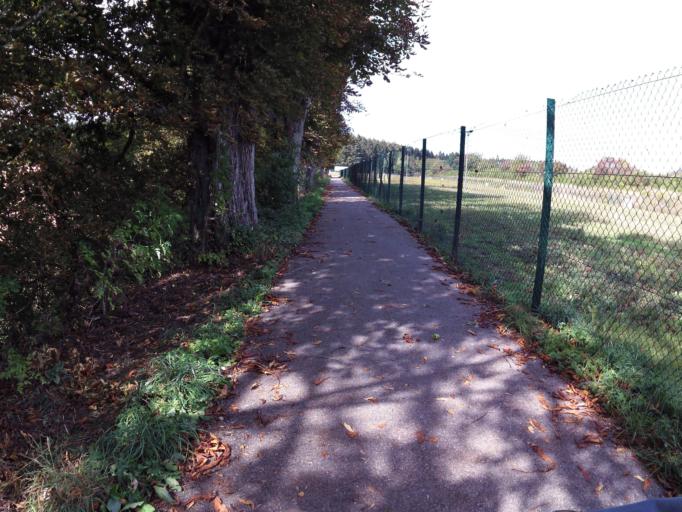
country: DE
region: Rheinland-Pfalz
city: Arzfeld
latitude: 50.0929
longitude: 6.2746
